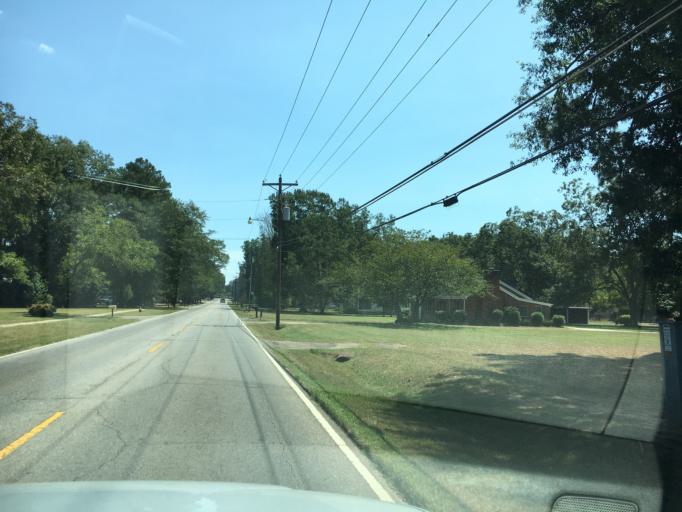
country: US
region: South Carolina
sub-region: Edgefield County
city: Johnston
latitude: 33.8472
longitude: -81.6696
